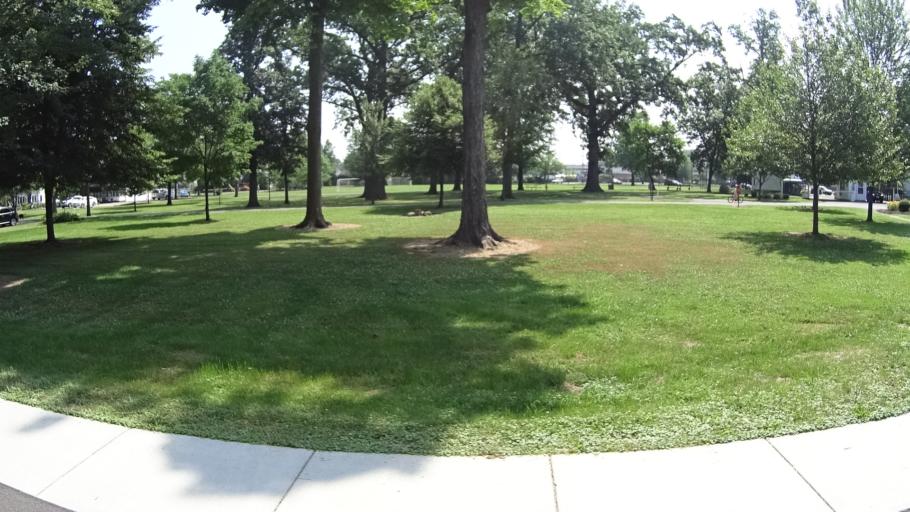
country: US
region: Ohio
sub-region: Lorain County
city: Vermilion
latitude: 41.4244
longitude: -82.3547
